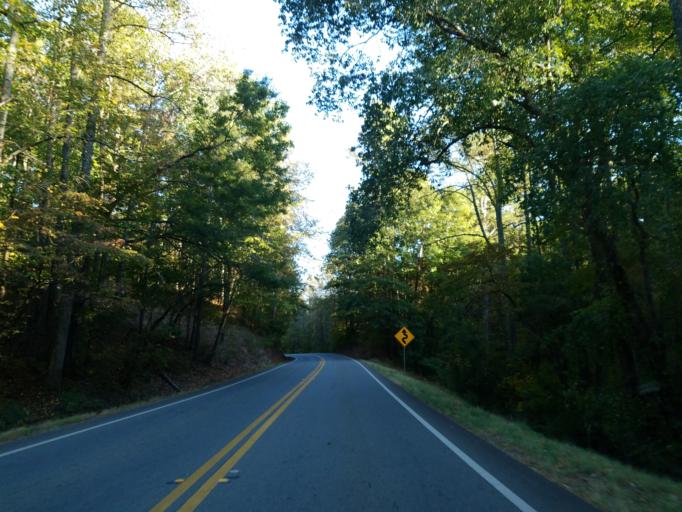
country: US
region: Georgia
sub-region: Dawson County
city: Dawsonville
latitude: 34.4304
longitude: -84.1749
